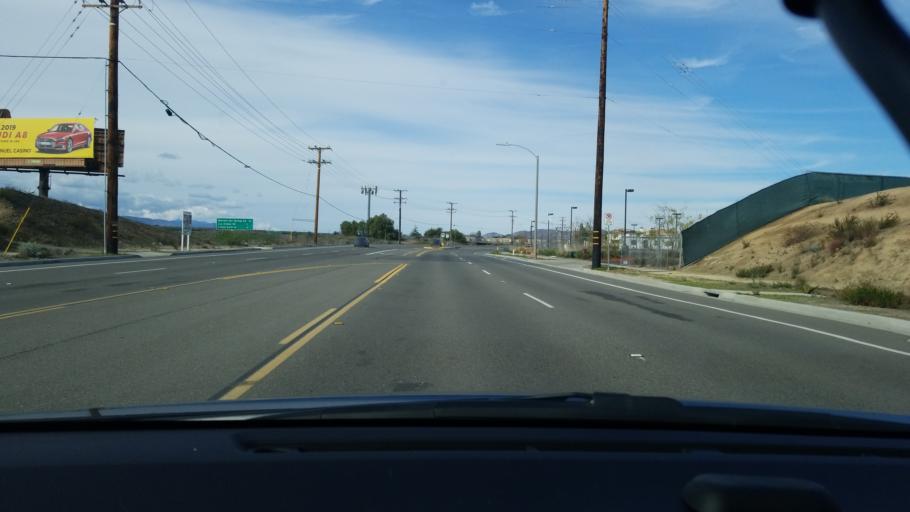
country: US
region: California
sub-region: Riverside County
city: Murrieta Hot Springs
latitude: 33.5469
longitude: -117.1774
